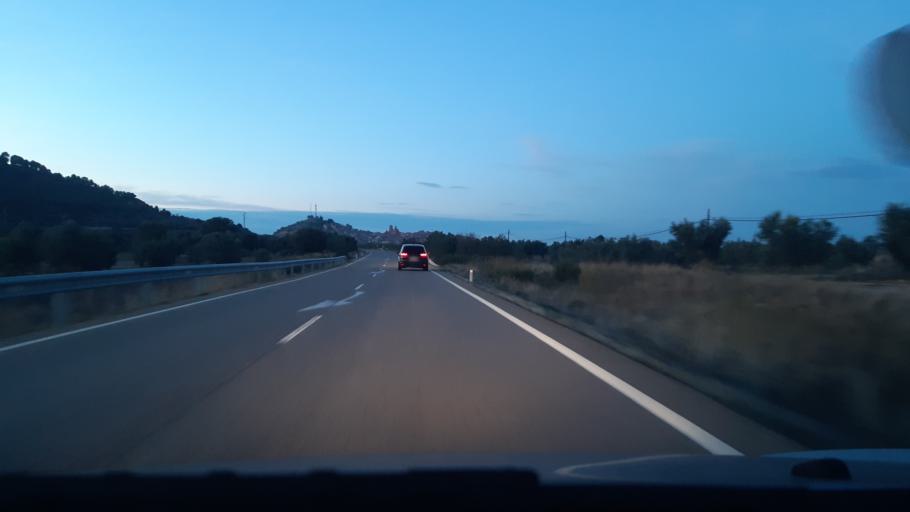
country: ES
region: Aragon
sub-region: Provincia de Teruel
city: Calaceite
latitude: 41.0039
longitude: 0.1929
